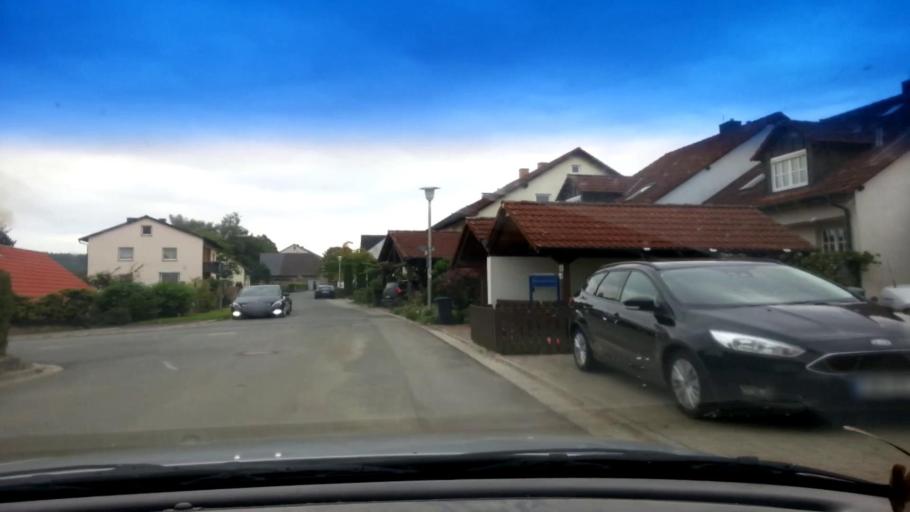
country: DE
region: Bavaria
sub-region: Upper Franconia
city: Zapfendorf
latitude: 50.0035
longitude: 10.9395
